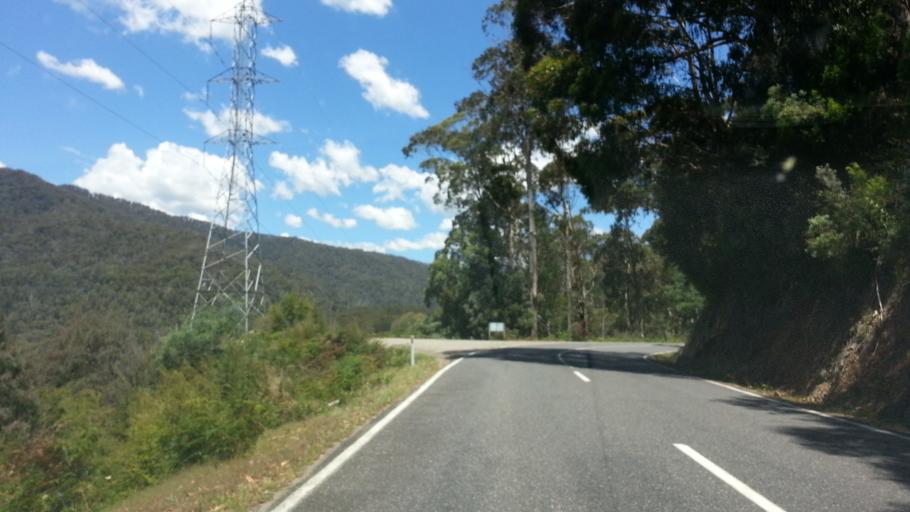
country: AU
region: Victoria
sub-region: Alpine
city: Mount Beauty
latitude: -36.7690
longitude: 147.2137
